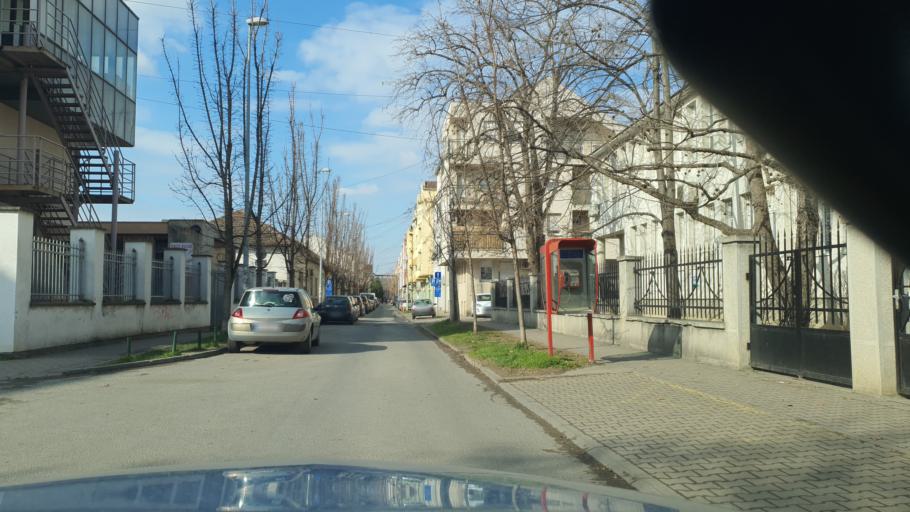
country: RS
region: Autonomna Pokrajina Vojvodina
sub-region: Juznobacki Okrug
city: Novi Sad
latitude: 45.2587
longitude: 19.8293
